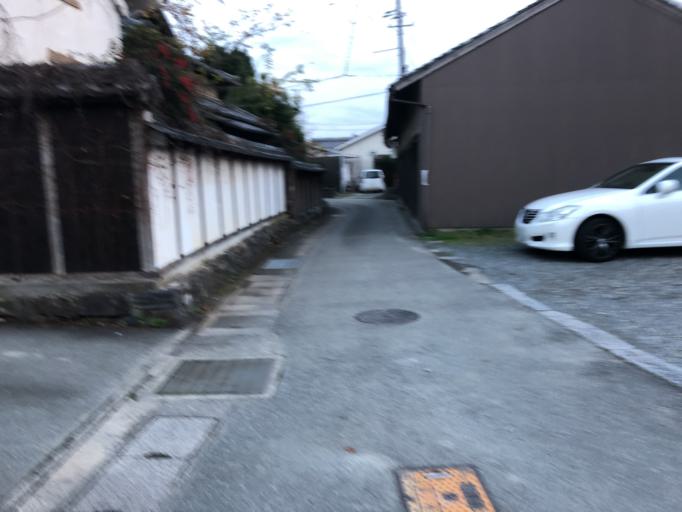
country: JP
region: Kyoto
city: Kameoka
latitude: 35.0575
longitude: 135.5619
